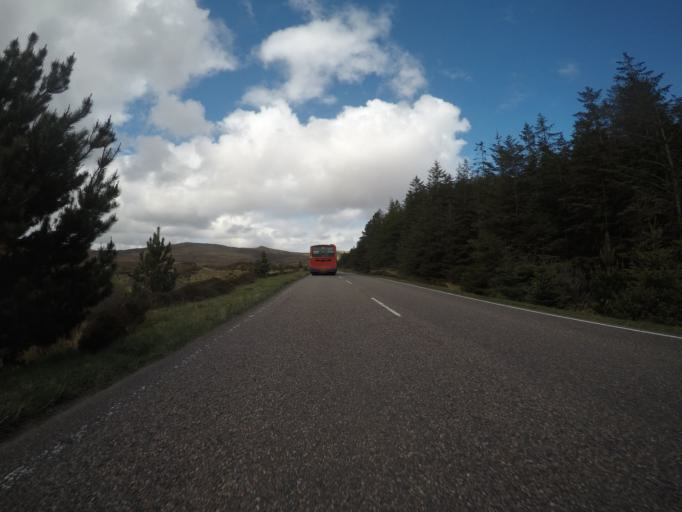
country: GB
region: Scotland
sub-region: Highland
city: Isle of Skye
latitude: 57.3174
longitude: -6.2021
